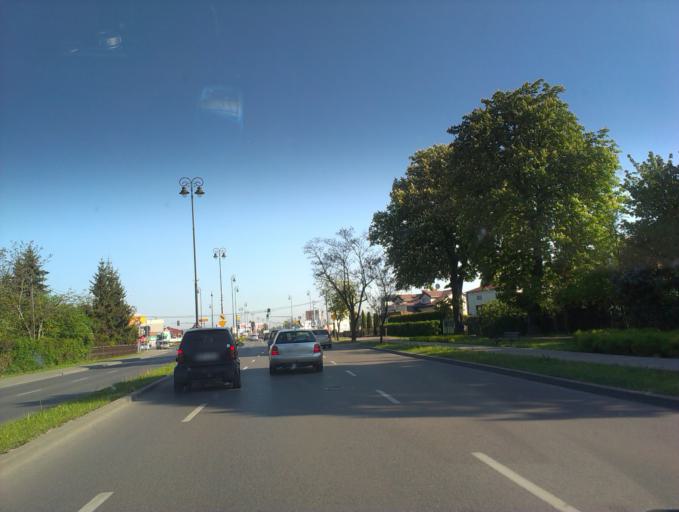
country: PL
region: Masovian Voivodeship
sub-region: Powiat piaseczynski
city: Konstancin-Jeziorna
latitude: 52.1041
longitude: 21.1141
